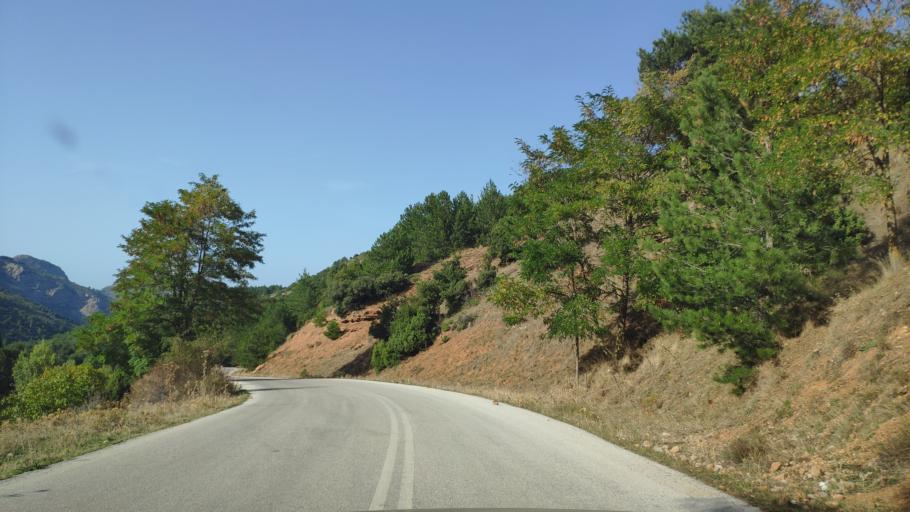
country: GR
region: West Greece
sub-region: Nomos Achaias
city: Aiyira
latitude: 38.0483
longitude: 22.3848
